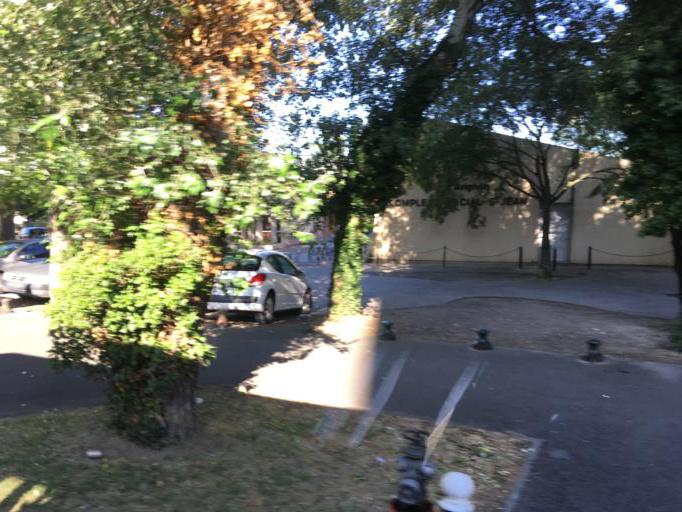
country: FR
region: Provence-Alpes-Cote d'Azur
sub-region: Departement du Vaucluse
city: Avignon
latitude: 43.9481
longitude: 4.8290
